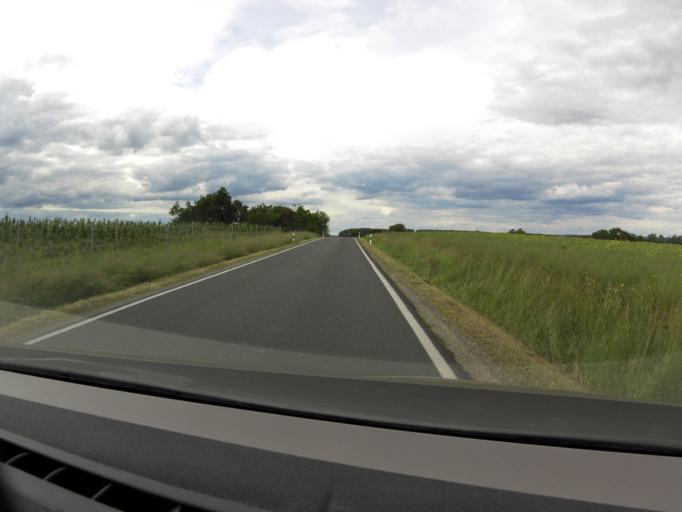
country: DE
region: Thuringia
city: Kammerforst
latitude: 51.1290
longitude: 10.4290
